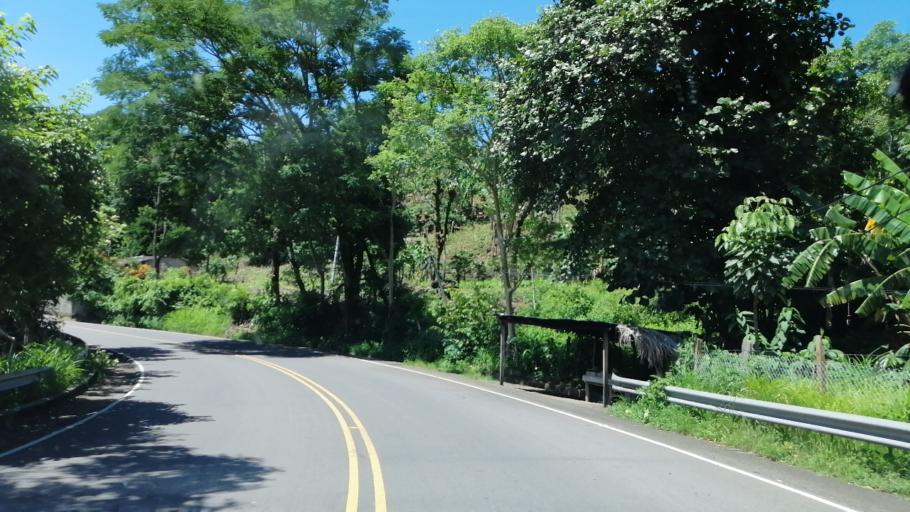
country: SV
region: San Miguel
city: Ciudad Barrios
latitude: 13.8057
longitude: -88.1915
